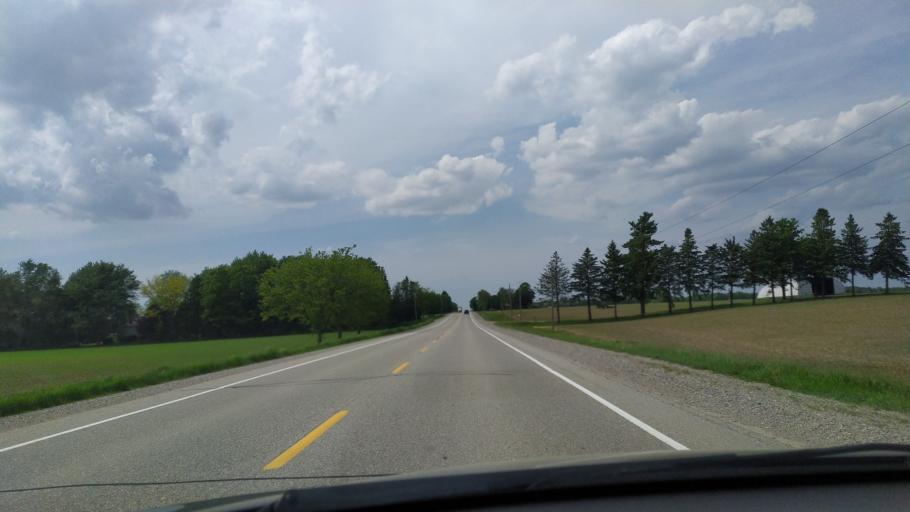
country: CA
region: Ontario
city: Dorchester
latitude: 43.1501
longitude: -81.0358
